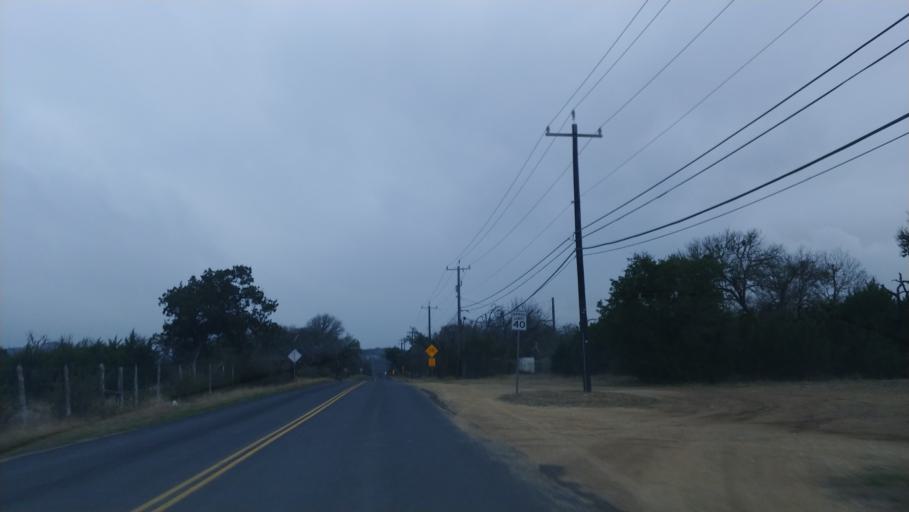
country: US
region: Texas
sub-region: Bexar County
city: Scenic Oaks
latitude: 29.6806
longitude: -98.6744
